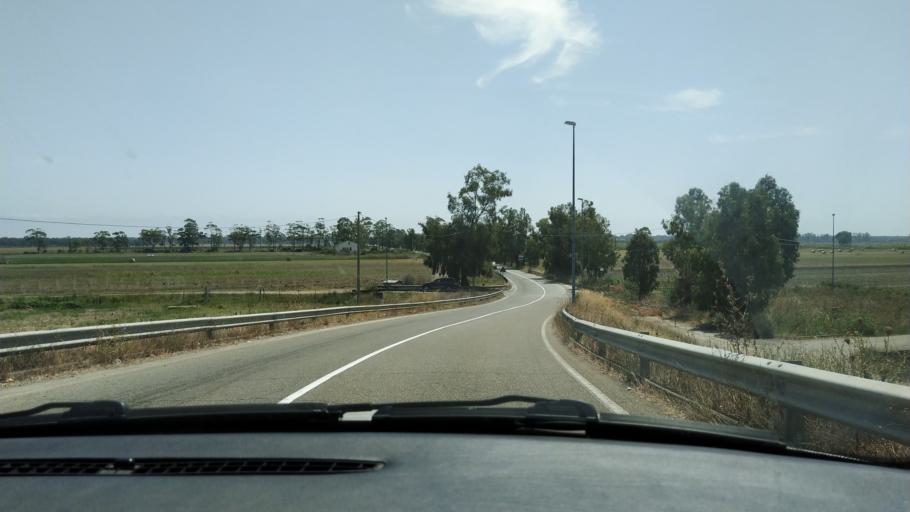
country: IT
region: Basilicate
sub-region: Provincia di Matera
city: Marconia
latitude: 40.3349
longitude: 16.7756
